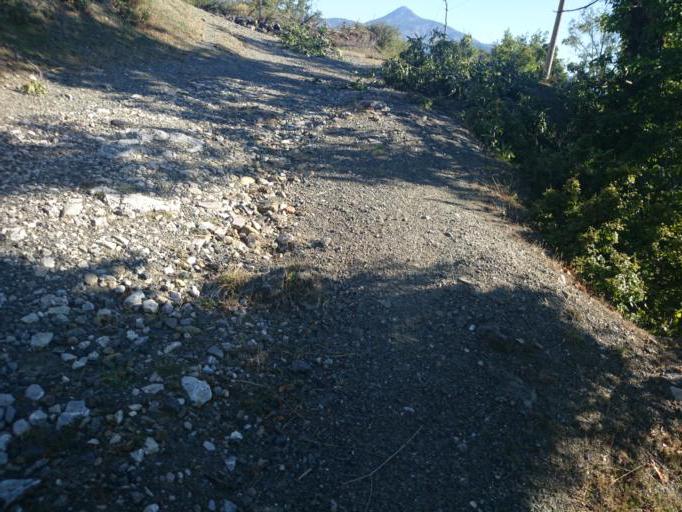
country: AL
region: Elbasan
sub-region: Rrethi i Gramshit
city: Kukur
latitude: 40.8655
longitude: 20.3568
